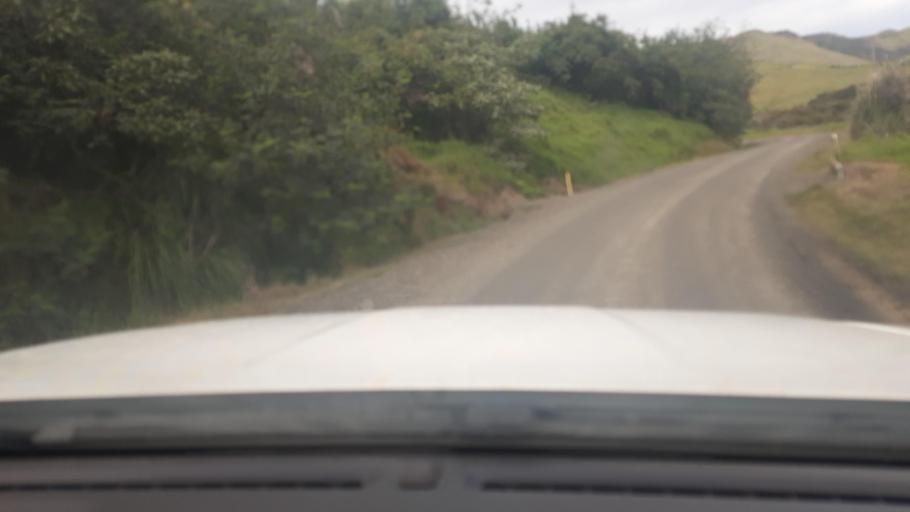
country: NZ
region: Northland
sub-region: Far North District
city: Ahipara
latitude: -35.2942
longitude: 173.2031
